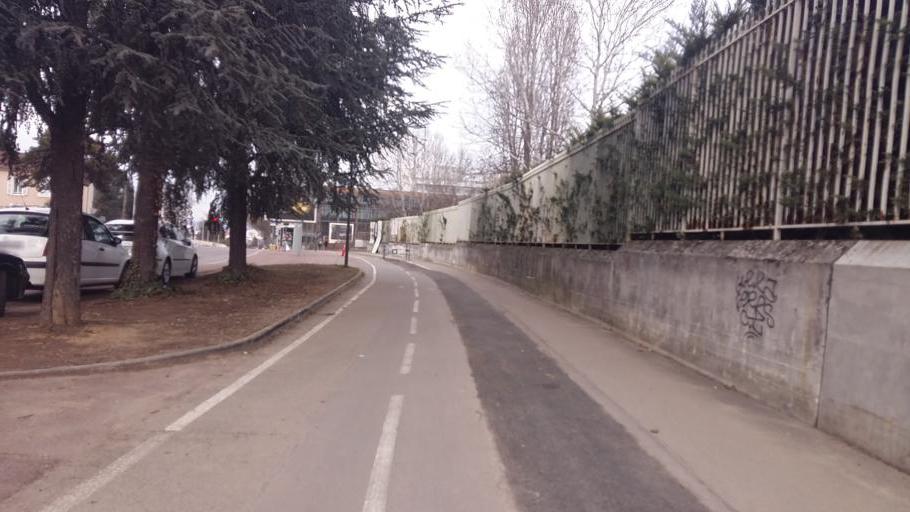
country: FR
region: Rhone-Alpes
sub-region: Departement du Rhone
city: Villeurbanne
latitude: 45.7467
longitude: 4.8966
